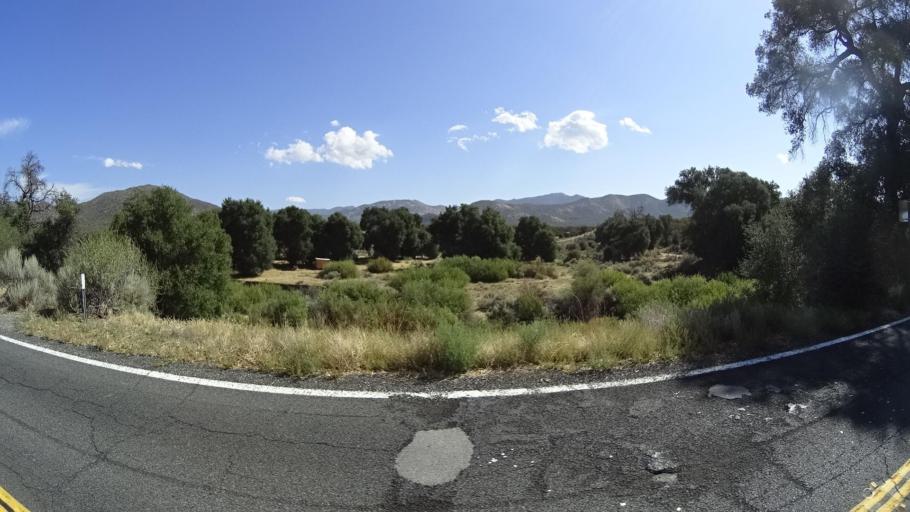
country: US
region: California
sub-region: Riverside County
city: Aguanga
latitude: 33.3217
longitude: -116.6992
